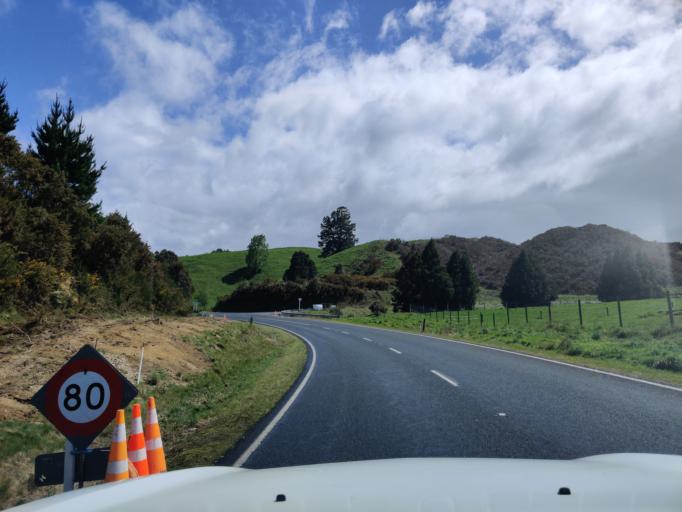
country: NZ
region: Bay of Plenty
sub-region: Rotorua District
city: Rotorua
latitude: -38.1694
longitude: 176.3210
